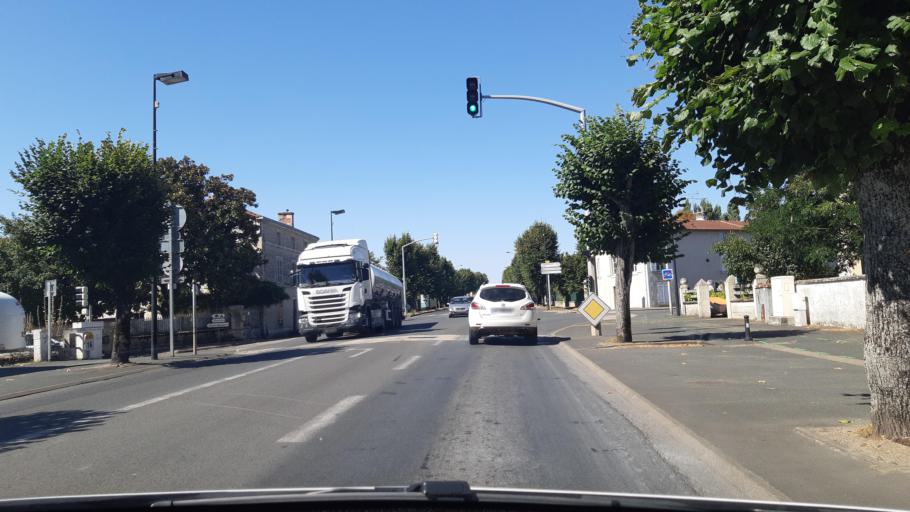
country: FR
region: Poitou-Charentes
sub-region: Departement des Deux-Sevres
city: Saivres
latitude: 46.4103
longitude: -0.2157
